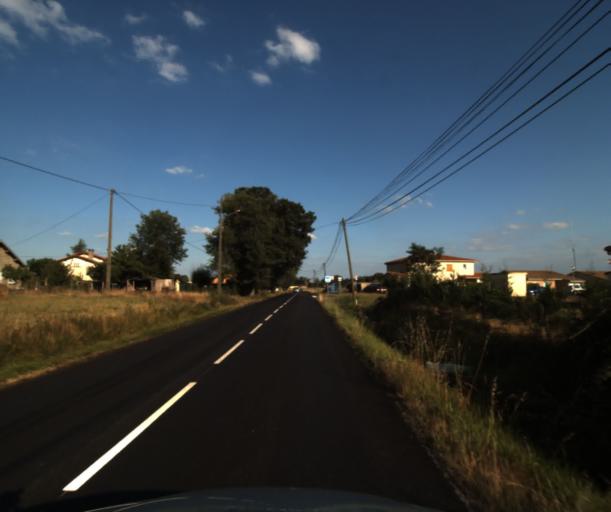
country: FR
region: Midi-Pyrenees
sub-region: Departement de la Haute-Garonne
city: Saint-Lys
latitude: 43.5040
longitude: 1.1887
